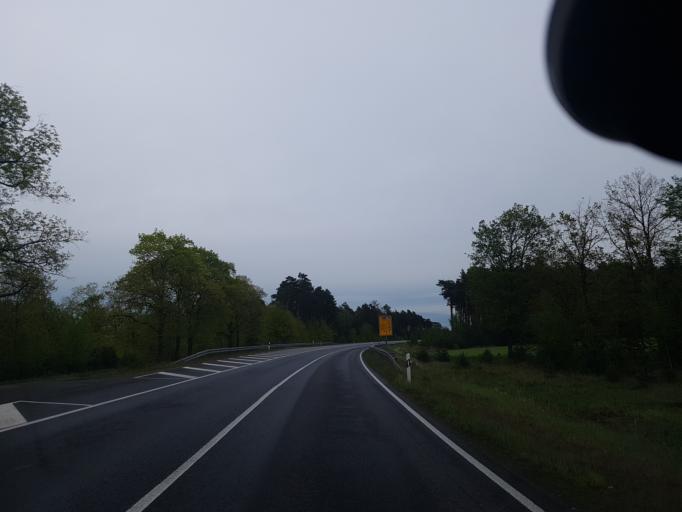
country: DE
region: Brandenburg
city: Neupetershain
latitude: 51.6318
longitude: 14.1780
